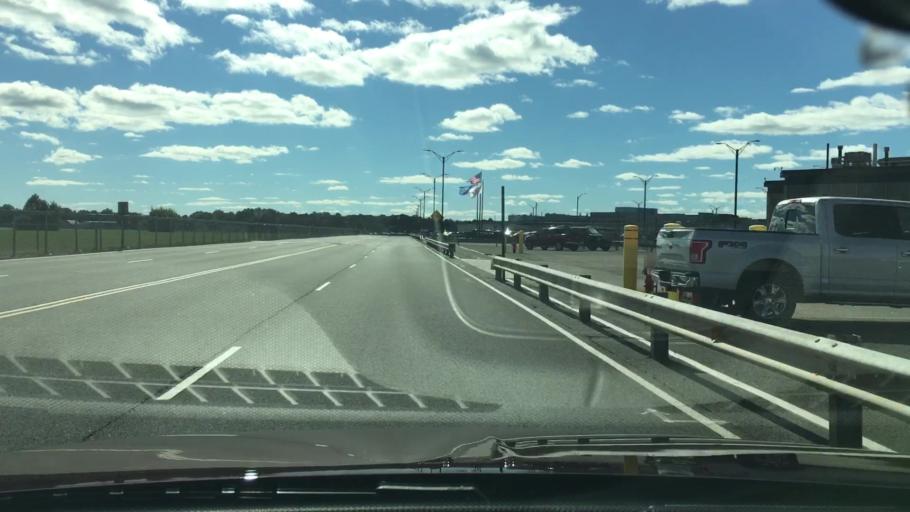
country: US
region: Connecticut
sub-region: Hartford County
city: East Hartford
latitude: 41.7510
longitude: -72.6269
